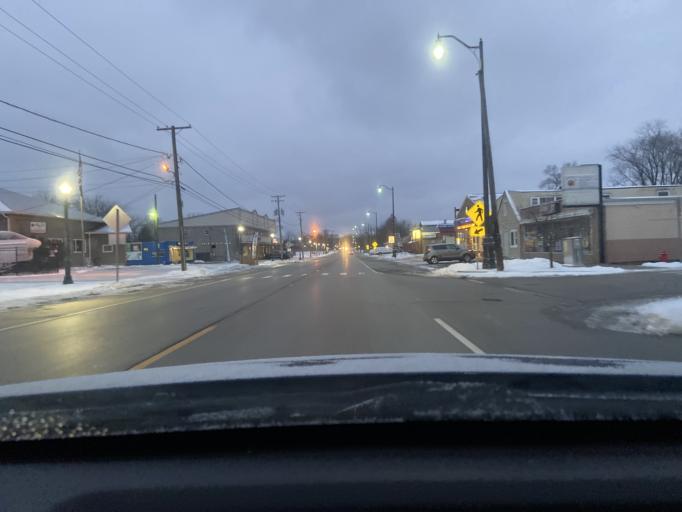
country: US
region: Illinois
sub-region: Lake County
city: Round Lake Park
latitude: 42.3492
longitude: -88.0803
